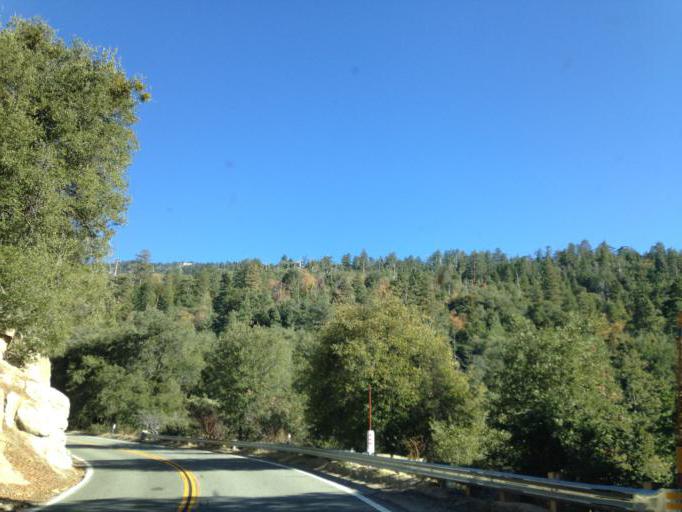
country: US
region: California
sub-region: Riverside County
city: Idyllwild-Pine Cove
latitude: 33.7947
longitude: -116.7456
